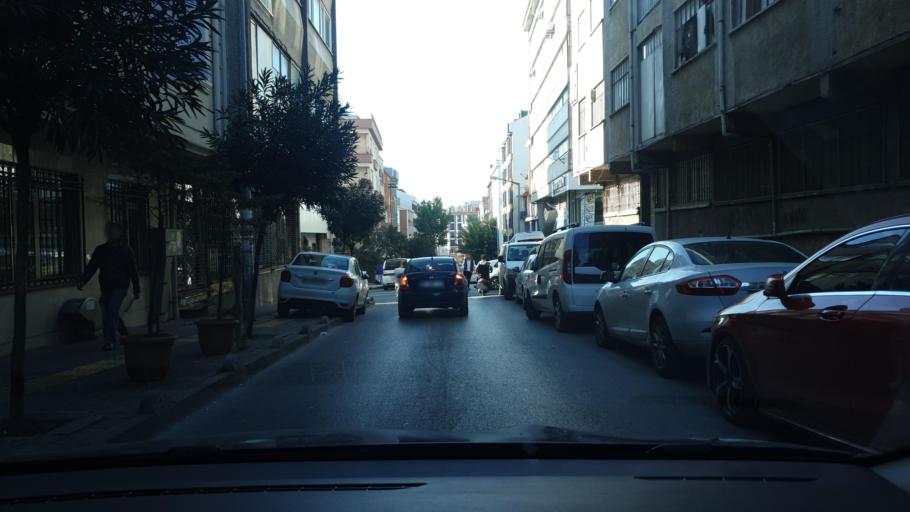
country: TR
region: Istanbul
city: Bahcelievler
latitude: 40.9941
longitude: 28.8416
